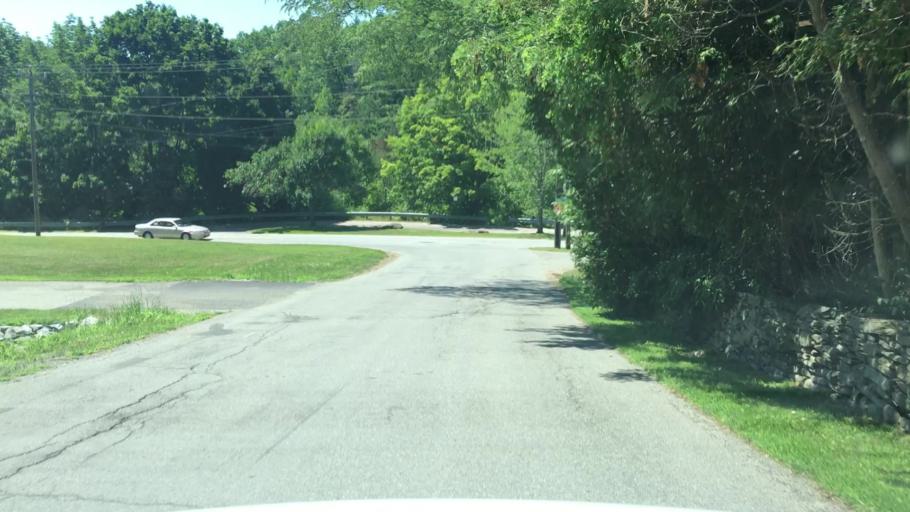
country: US
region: Maine
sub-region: Penobscot County
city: Bangor
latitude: 44.8162
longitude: -68.7892
